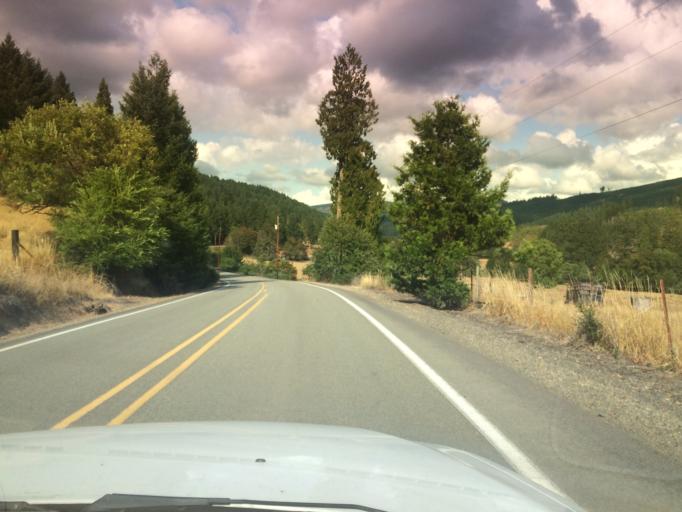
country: US
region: Oregon
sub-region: Douglas County
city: Sutherlin
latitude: 43.3666
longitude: -123.5751
